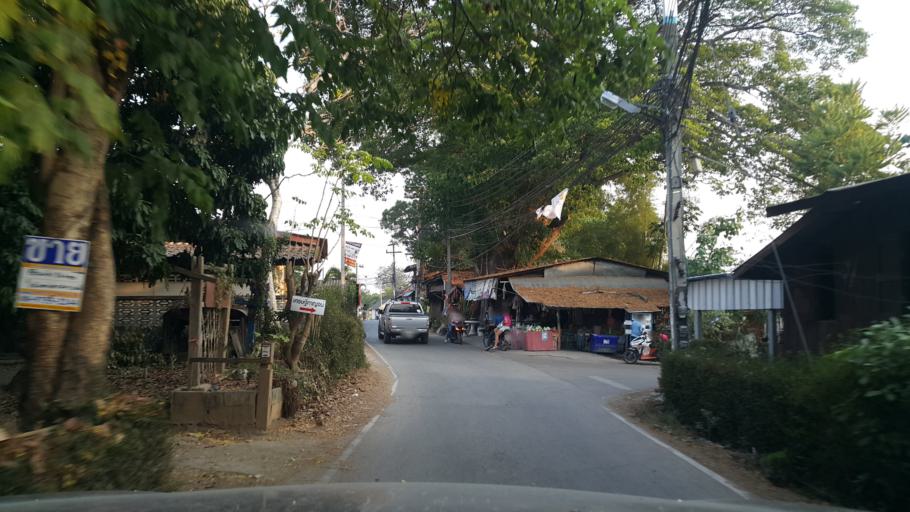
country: TH
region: Chiang Mai
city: Saraphi
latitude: 18.7214
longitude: 99.0227
